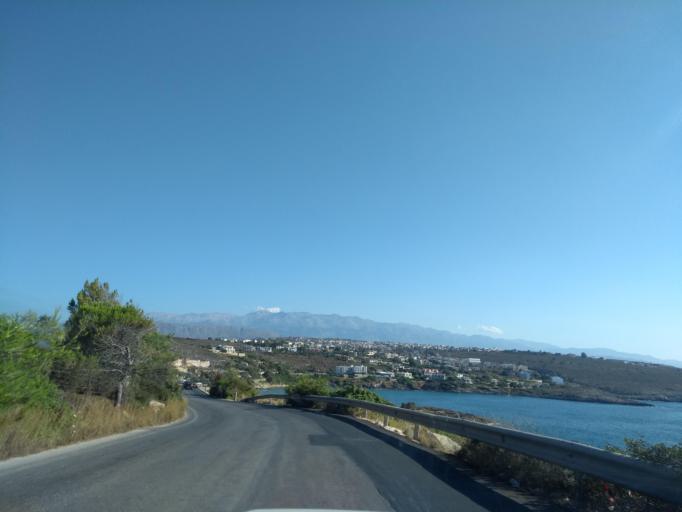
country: GR
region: Crete
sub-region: Nomos Chanias
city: Pithari
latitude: 35.5587
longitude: 24.0870
